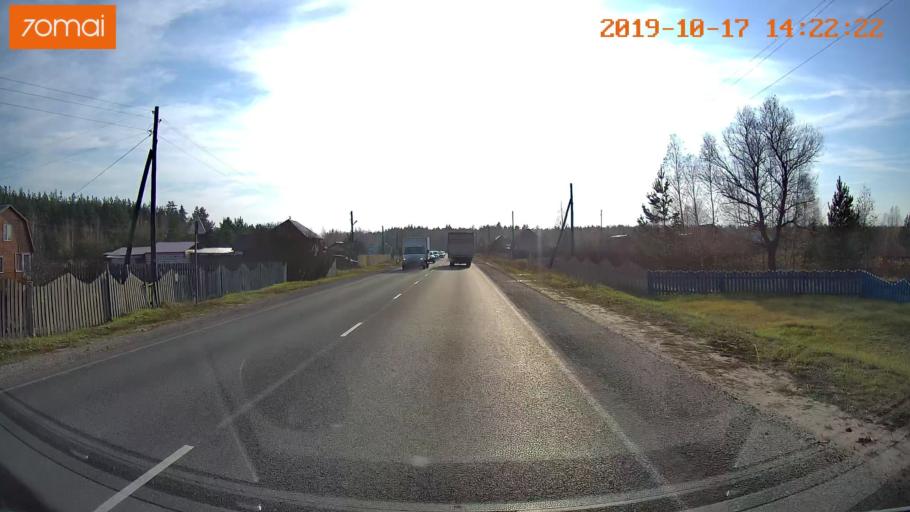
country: RU
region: Moskovskaya
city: Radovitskiy
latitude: 55.0304
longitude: 39.9686
